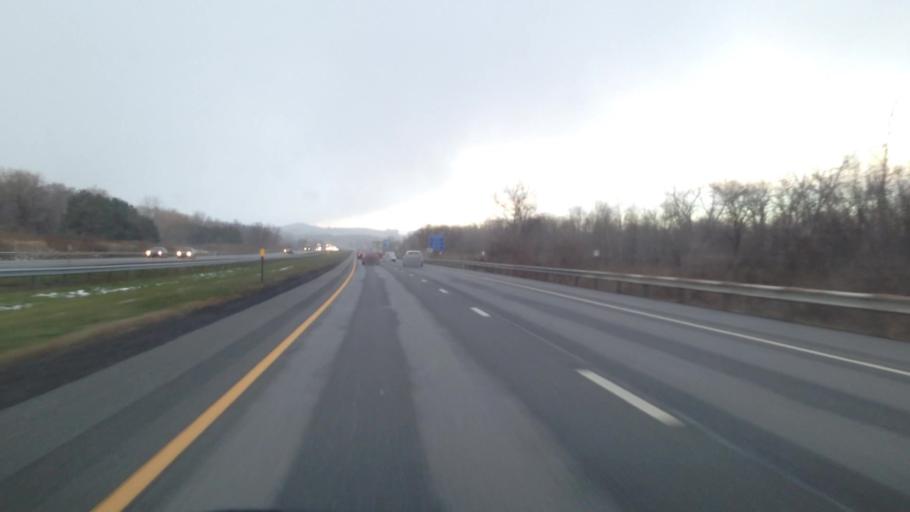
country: US
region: New York
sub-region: Montgomery County
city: Saint Johnsville
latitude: 43.0003
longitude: -74.7535
